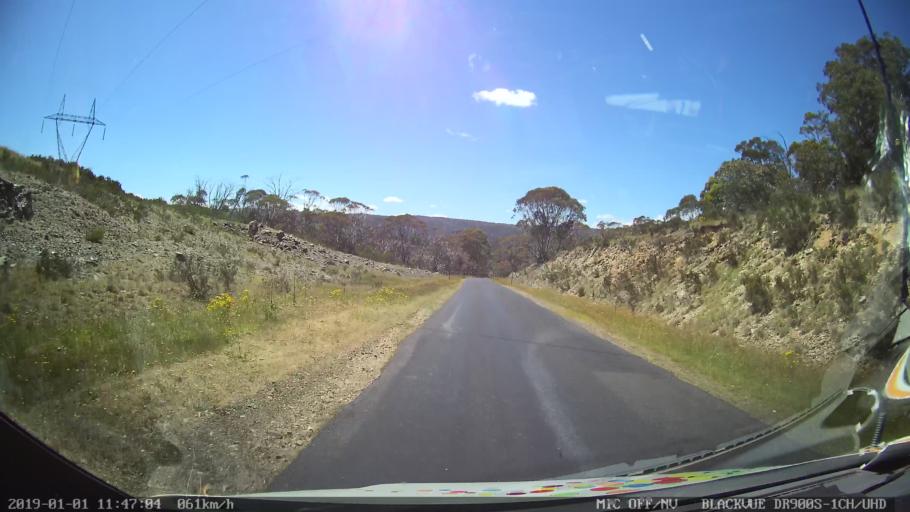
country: AU
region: New South Wales
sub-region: Snowy River
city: Jindabyne
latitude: -35.8896
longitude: 148.4013
